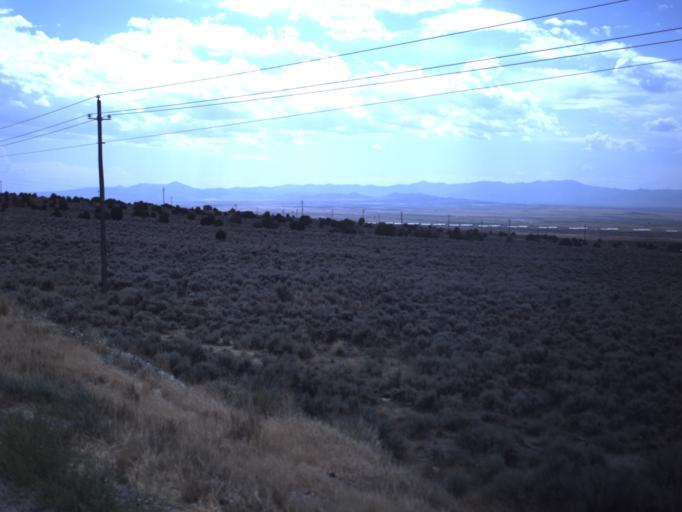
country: US
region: Utah
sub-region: Tooele County
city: Tooele
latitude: 40.3218
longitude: -112.2869
